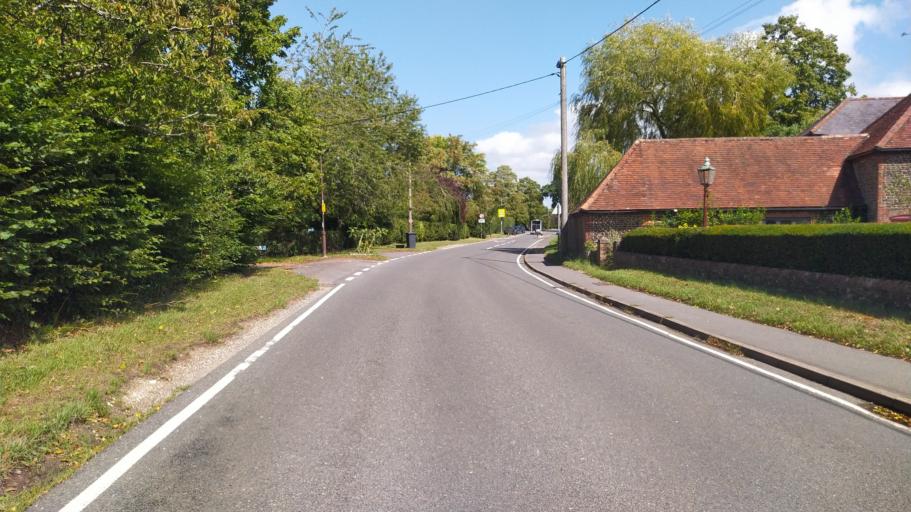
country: GB
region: England
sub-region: Hampshire
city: Liss
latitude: 51.0679
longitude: -0.8972
